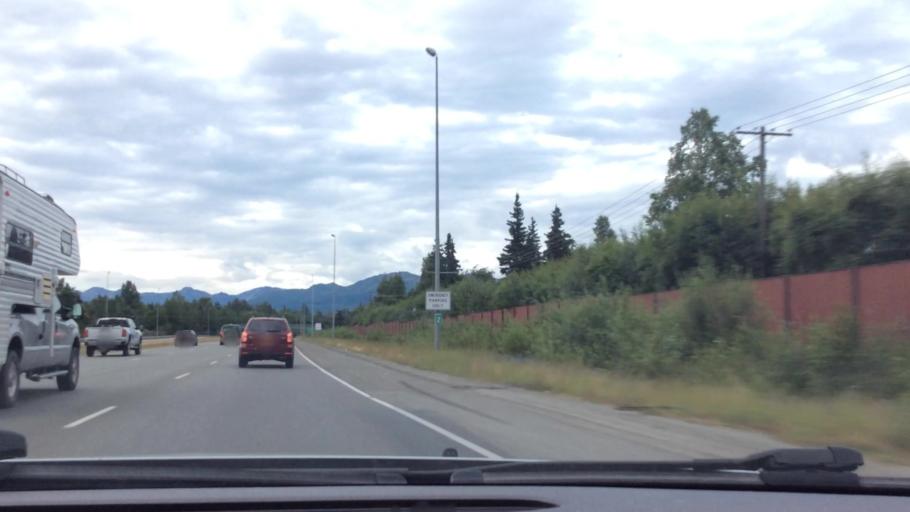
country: US
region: Alaska
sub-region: Anchorage Municipality
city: Anchorage
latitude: 61.2225
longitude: -149.8018
